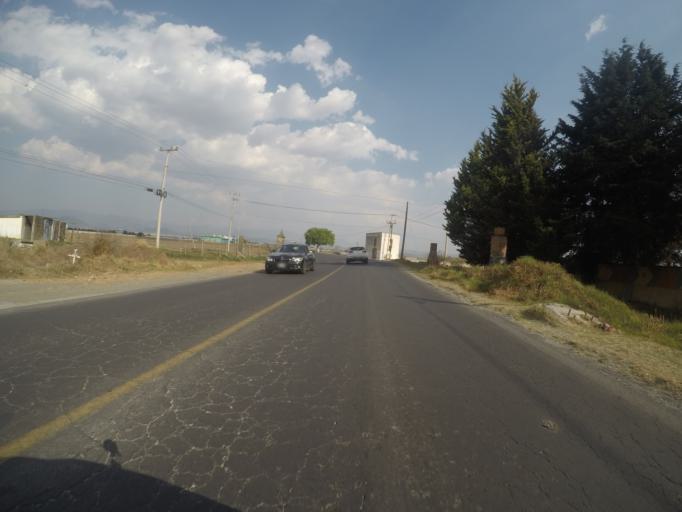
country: MX
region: Morelos
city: Chapultepec
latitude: 19.1925
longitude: -99.5370
